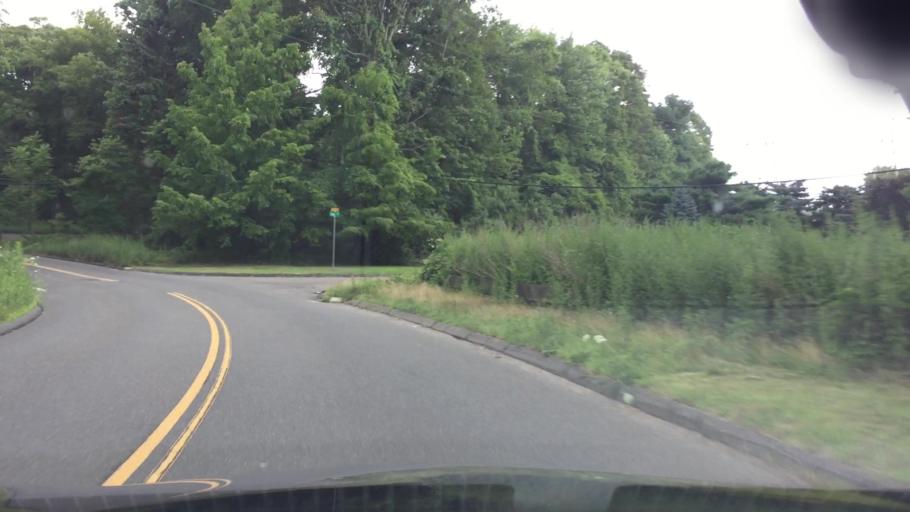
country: US
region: Connecticut
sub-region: Fairfield County
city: Shelton
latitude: 41.2624
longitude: -73.1191
